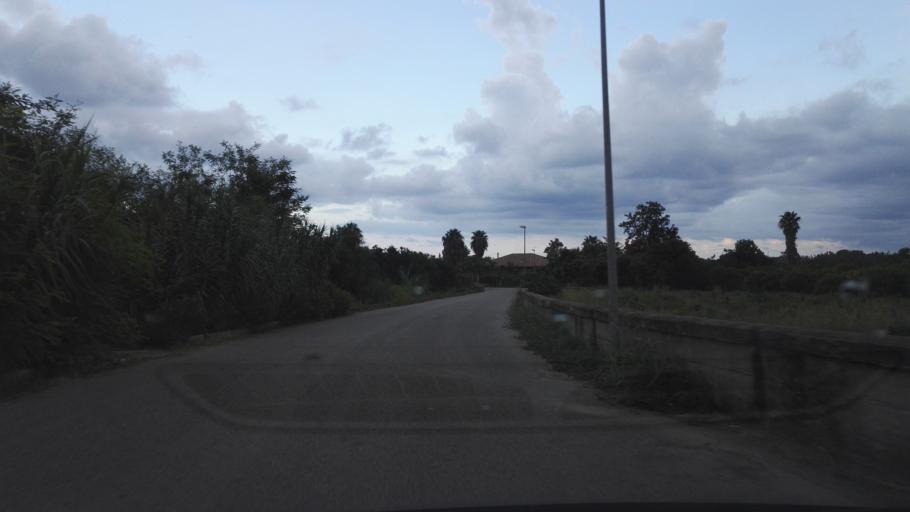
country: IT
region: Calabria
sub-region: Provincia di Reggio Calabria
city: Caulonia Marina
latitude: 38.3606
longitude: 16.4657
